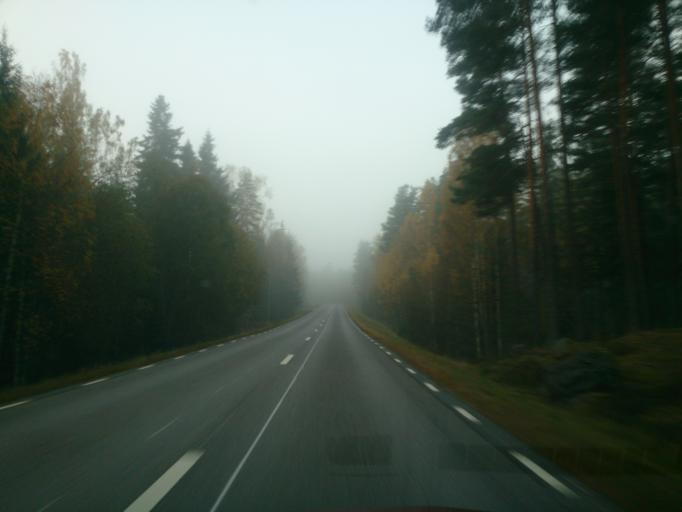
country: SE
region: OEstergoetland
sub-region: Atvidabergs Kommun
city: Atvidaberg
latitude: 58.1071
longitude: 15.9482
